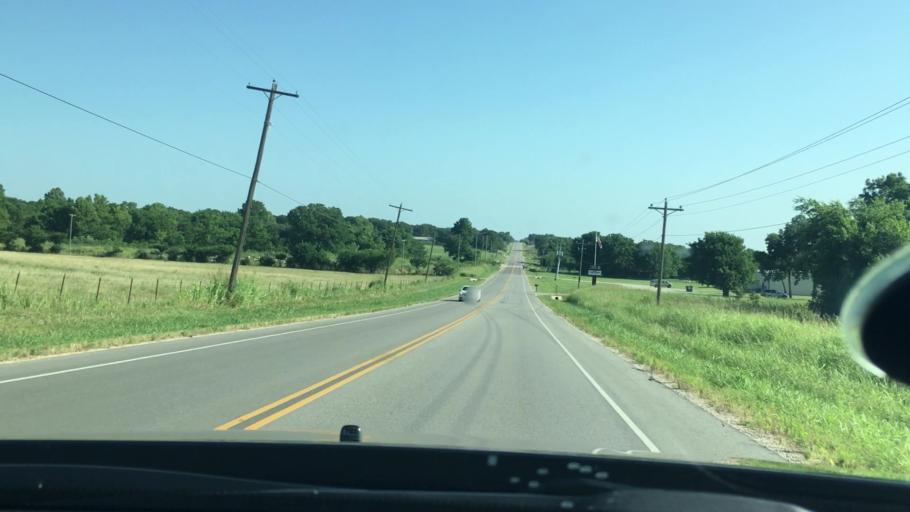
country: US
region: Oklahoma
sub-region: Pontotoc County
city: Ada
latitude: 34.7979
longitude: -96.6523
